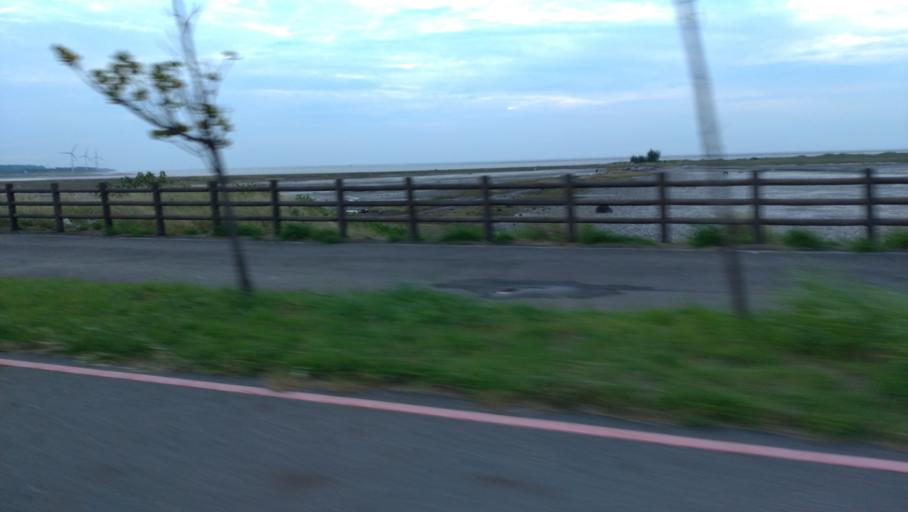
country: TW
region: Taiwan
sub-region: Hsinchu
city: Hsinchu
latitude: 24.7572
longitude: 120.9059
